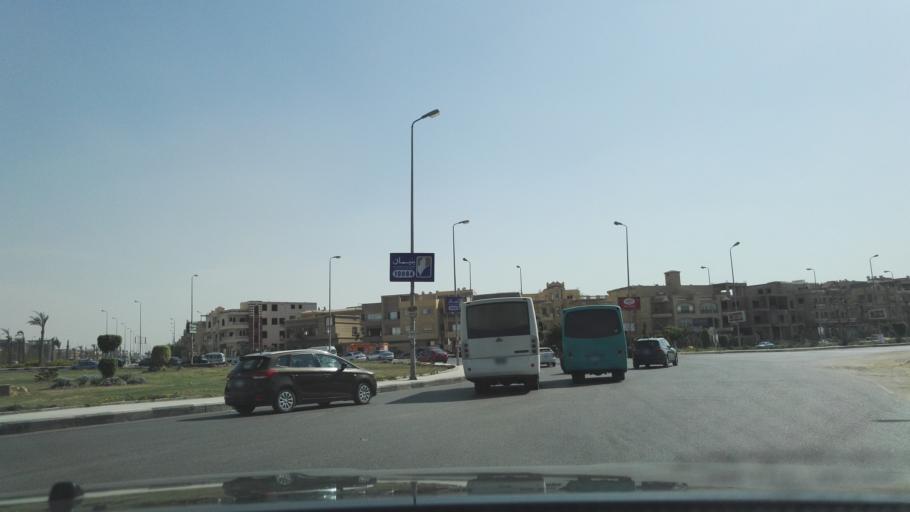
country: EG
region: Muhafazat al Qalyubiyah
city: Al Khankah
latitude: 30.0554
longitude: 31.4746
